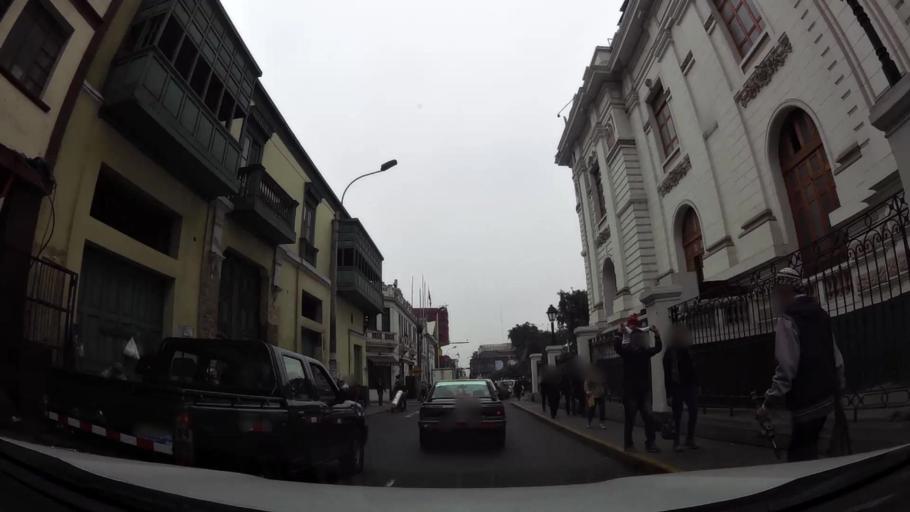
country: PE
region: Lima
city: Lima
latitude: -12.0484
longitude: -77.0256
